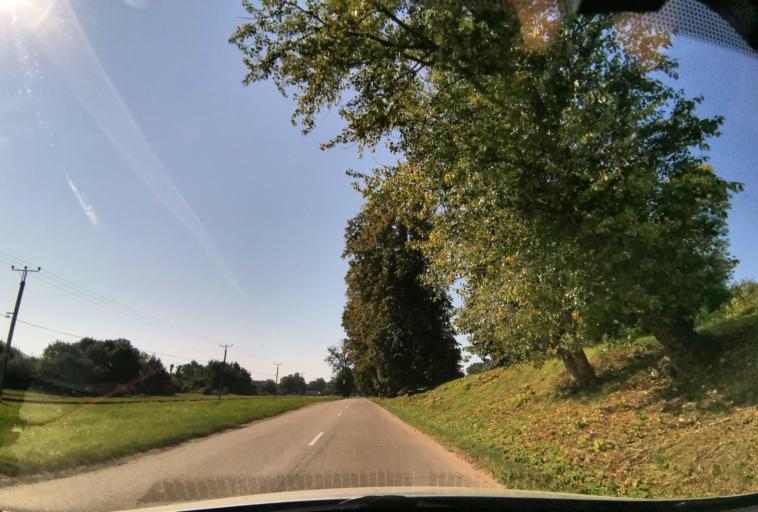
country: RU
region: Kaliningrad
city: Primorsk
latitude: 54.7321
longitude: 20.0026
